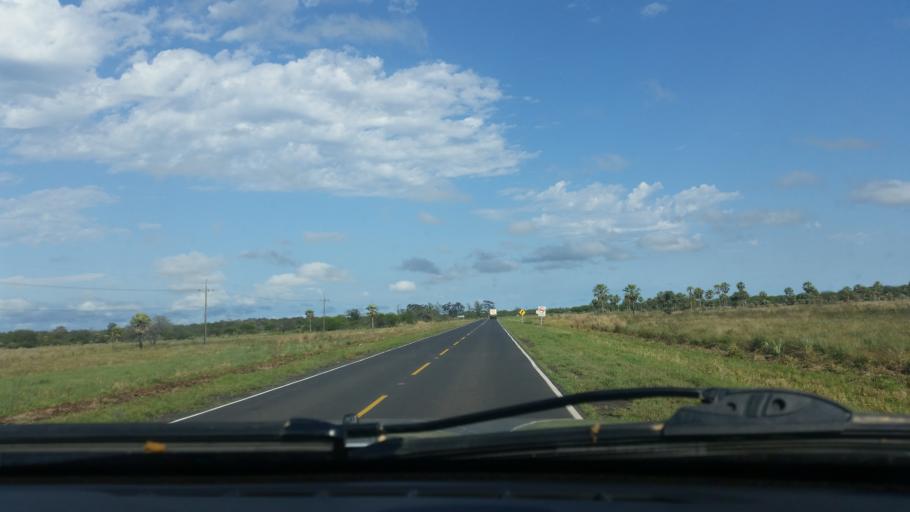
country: PY
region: Presidente Hayes
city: Benjamin Aceval
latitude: -24.9206
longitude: -57.5974
